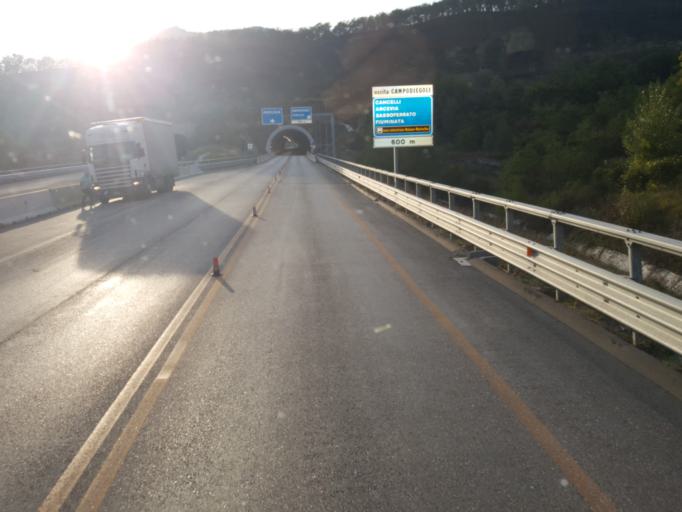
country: IT
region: Umbria
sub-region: Provincia di Perugia
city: Fossato di Vico
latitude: 43.3032
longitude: 12.8336
